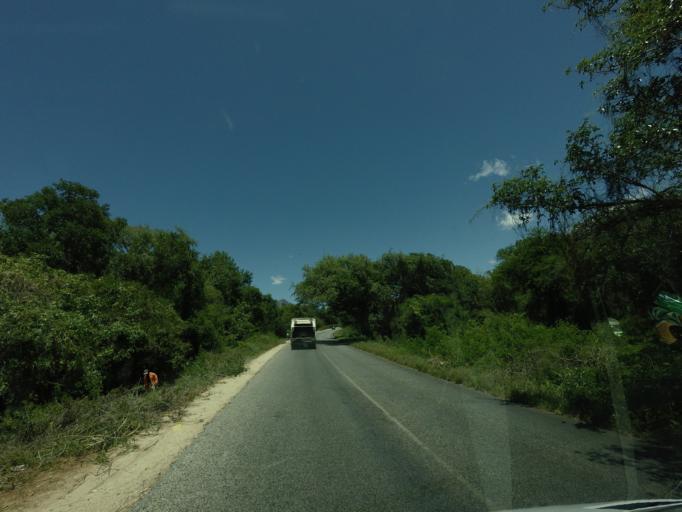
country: ZA
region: Limpopo
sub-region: Mopani District Municipality
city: Hoedspruit
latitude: -24.4073
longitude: 30.7950
